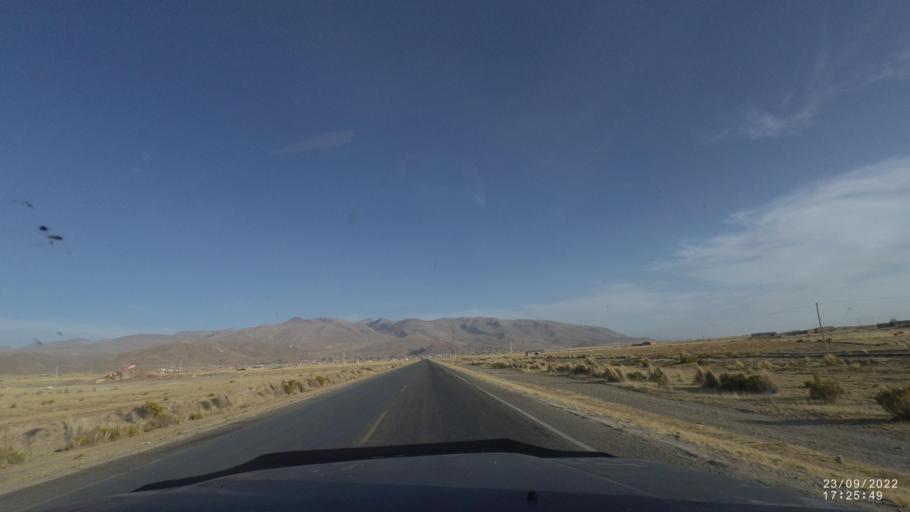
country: BO
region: Oruro
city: Challapata
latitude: -18.8761
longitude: -66.7929
